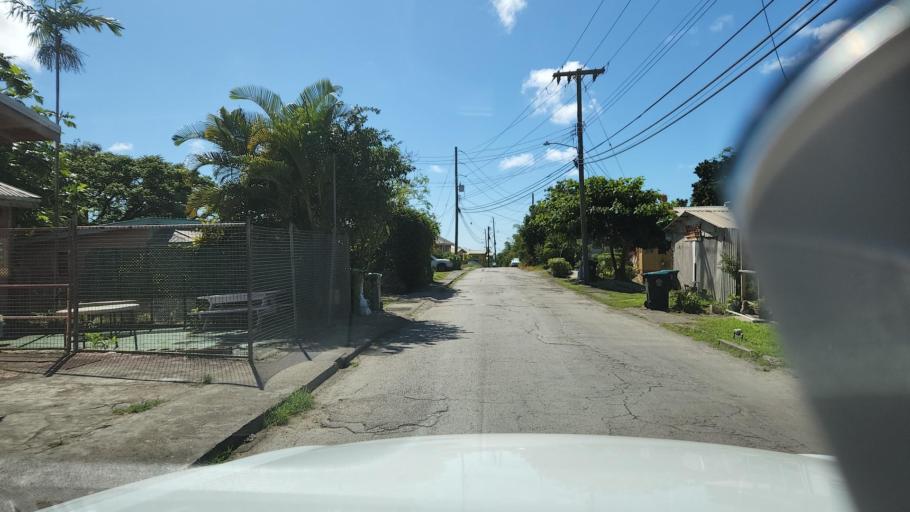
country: BB
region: Saint Thomas
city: Welchman Hall
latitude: 13.2129
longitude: -59.5885
